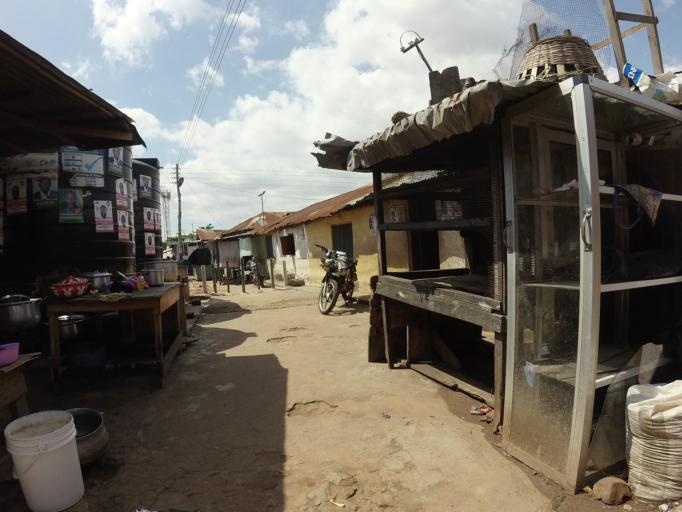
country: GH
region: Greater Accra
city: Accra
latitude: 5.5828
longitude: -0.1973
